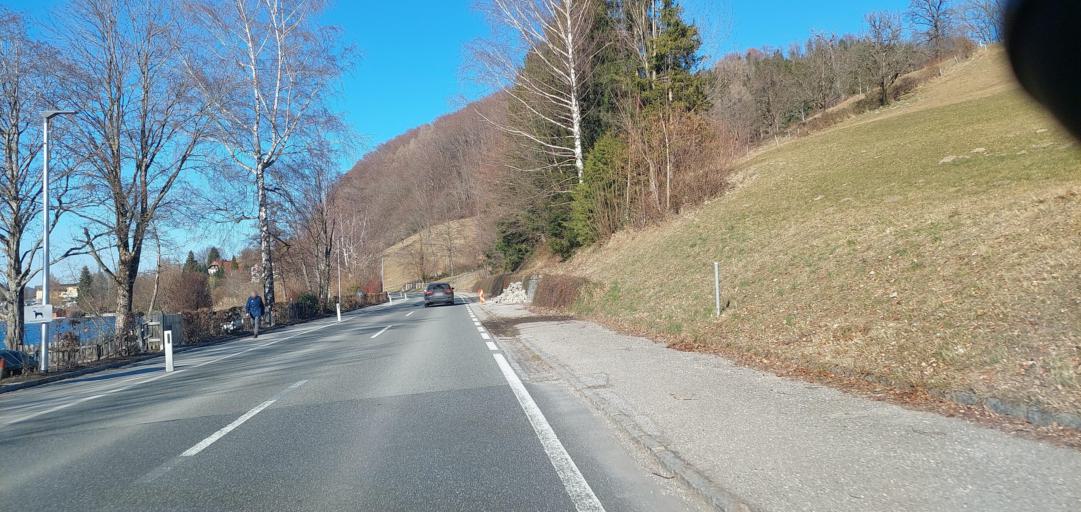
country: AT
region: Upper Austria
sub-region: Politischer Bezirk Vocklabruck
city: Steinbach am Attersee
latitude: 47.8319
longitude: 13.5463
